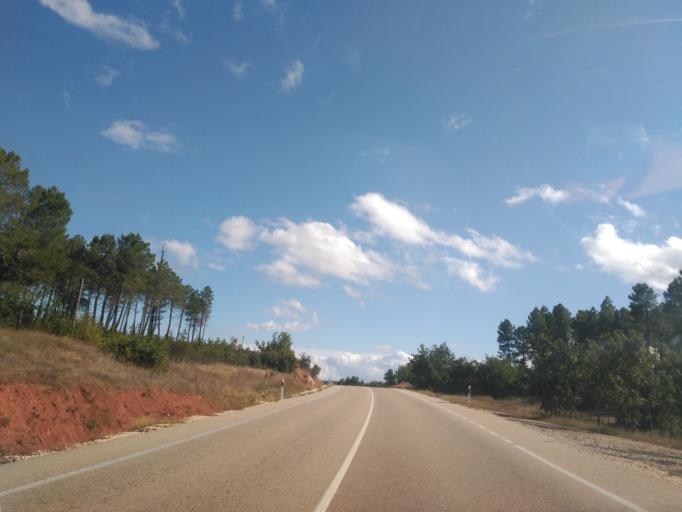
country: ES
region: Castille and Leon
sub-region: Provincia de Burgos
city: Pinilla de los Barruecos
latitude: 41.9439
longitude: -3.2914
